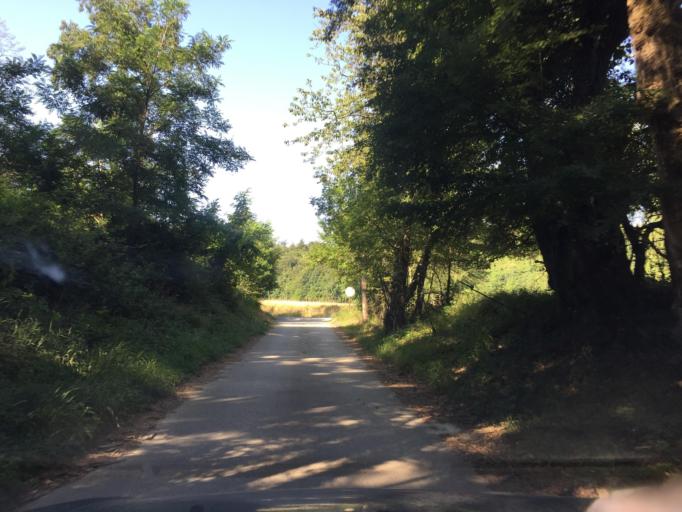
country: HR
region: Primorsko-Goranska
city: Klana
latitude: 45.4339
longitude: 14.3902
